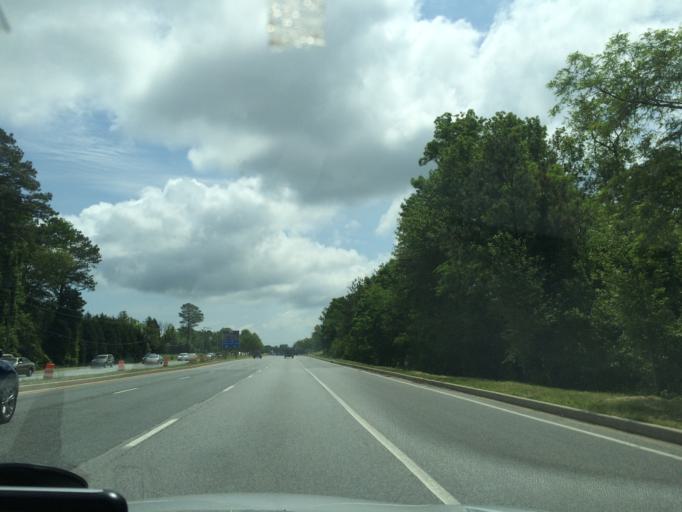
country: US
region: Maryland
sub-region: Saint Mary's County
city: California
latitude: 38.3058
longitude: -76.5254
